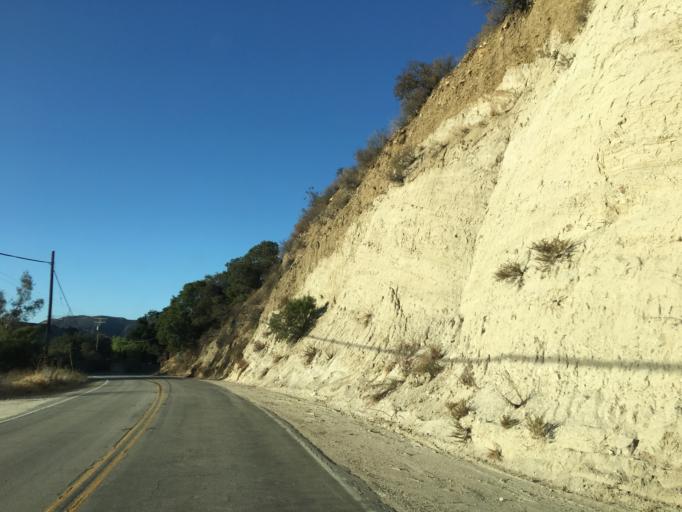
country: US
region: California
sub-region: Los Angeles County
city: San Fernando
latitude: 34.3073
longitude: -118.3468
